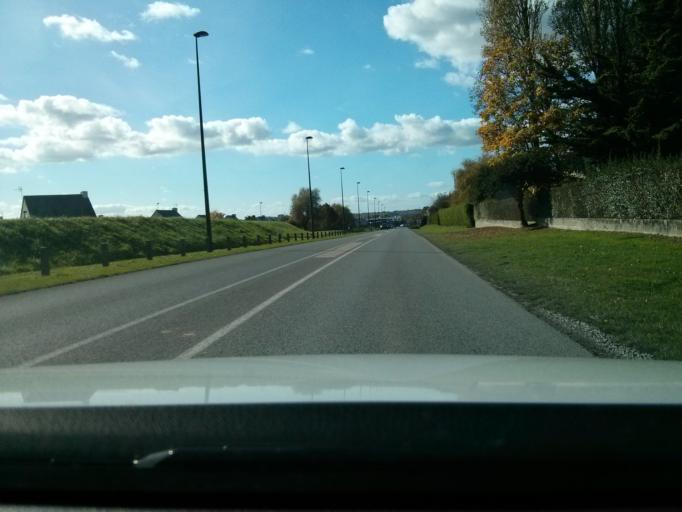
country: FR
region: Brittany
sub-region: Departement des Cotes-d'Armor
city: Ploubalay
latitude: 48.5791
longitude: -2.1456
